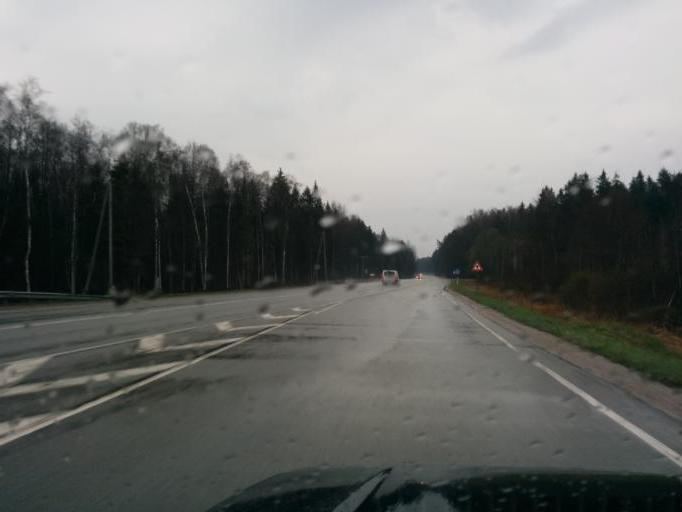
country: LV
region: Marupe
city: Marupe
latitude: 56.8318
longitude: 24.0447
